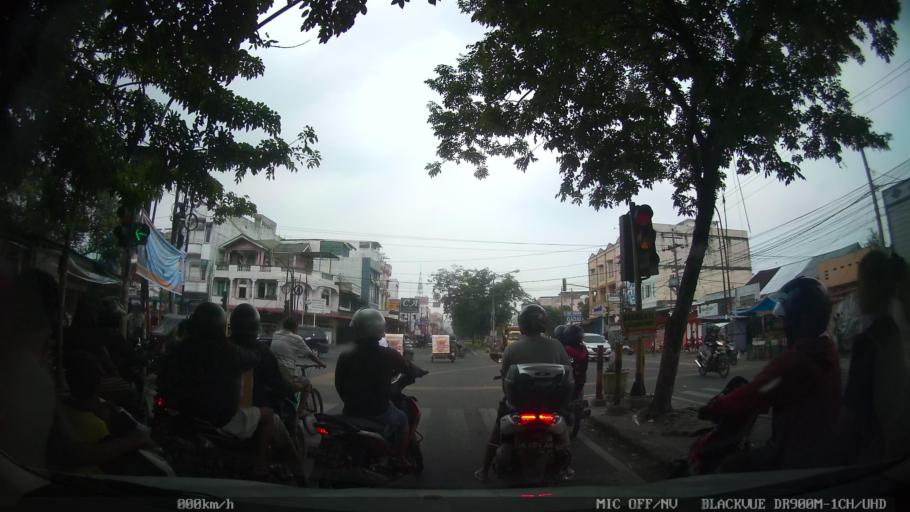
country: ID
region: North Sumatra
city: Medan
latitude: 3.5721
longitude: 98.7033
